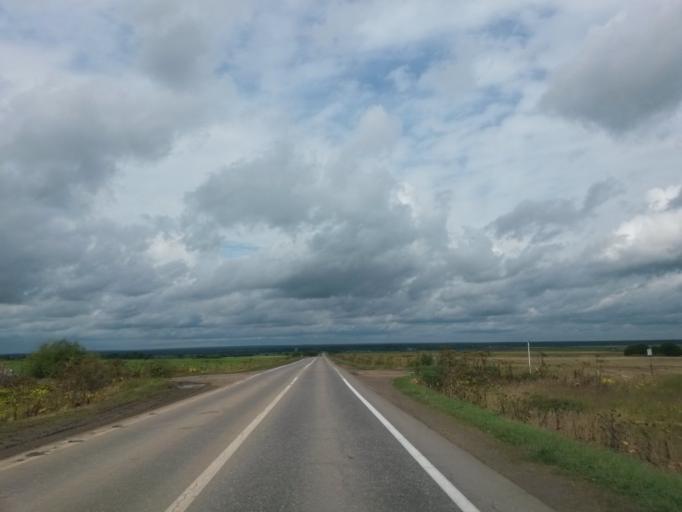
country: RU
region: Jaroslavl
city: Yaroslavl
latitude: 57.7613
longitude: 39.8653
